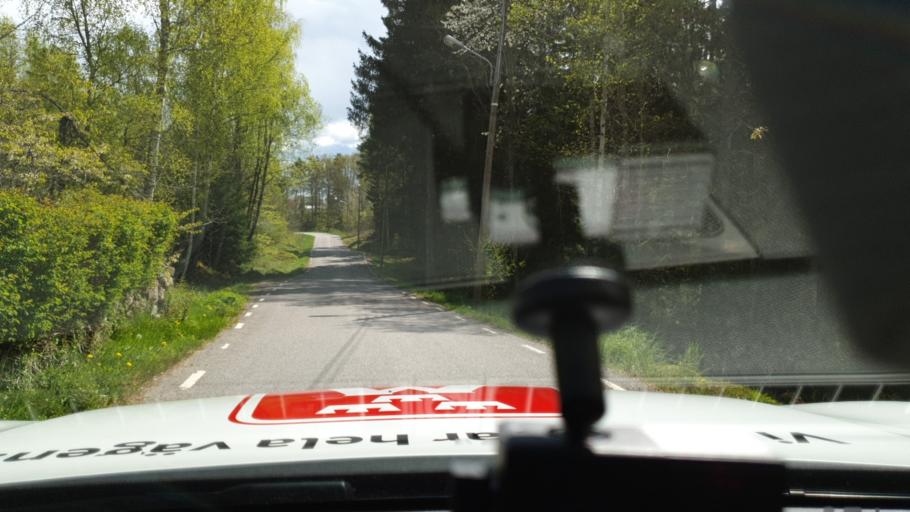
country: SE
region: Kalmar
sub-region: Vasterviks Kommun
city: Ankarsrum
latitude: 57.7829
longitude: 16.1463
